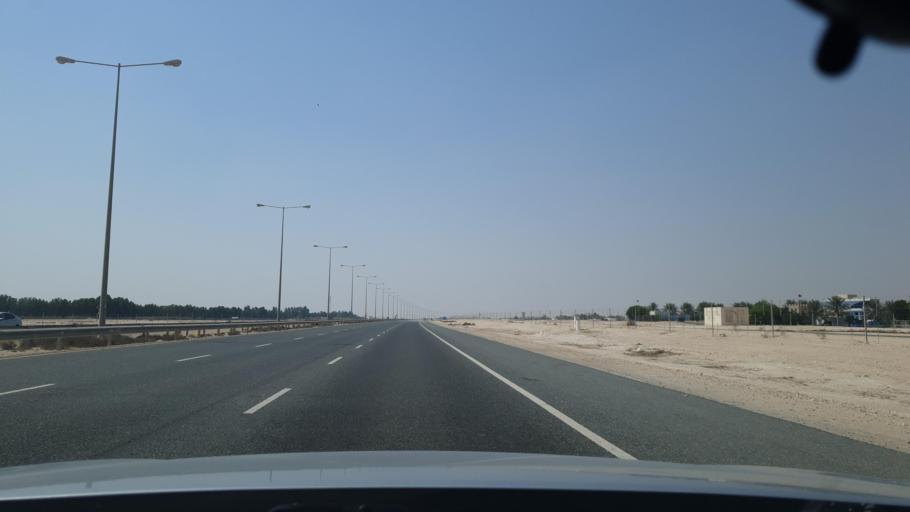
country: QA
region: Al Khawr
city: Al Khawr
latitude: 25.7564
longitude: 51.4585
